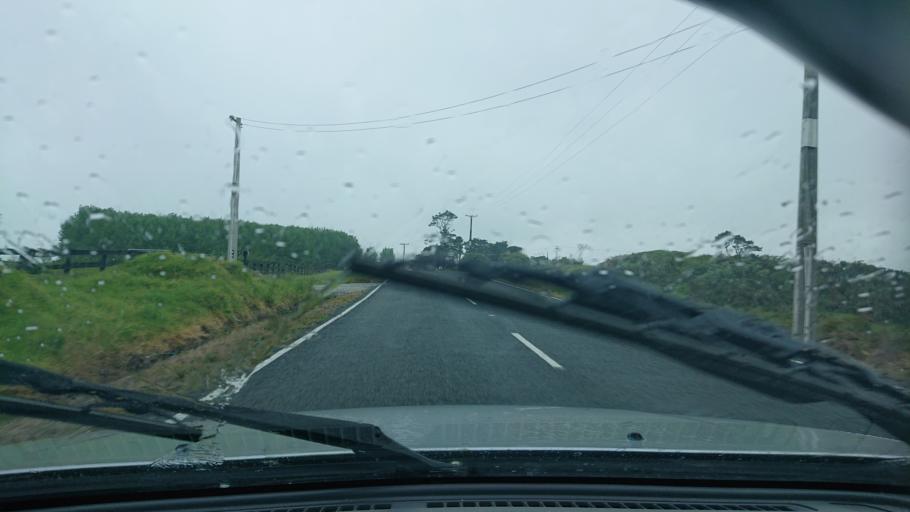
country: NZ
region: Auckland
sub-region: Auckland
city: Wellsford
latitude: -36.3284
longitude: 174.4070
